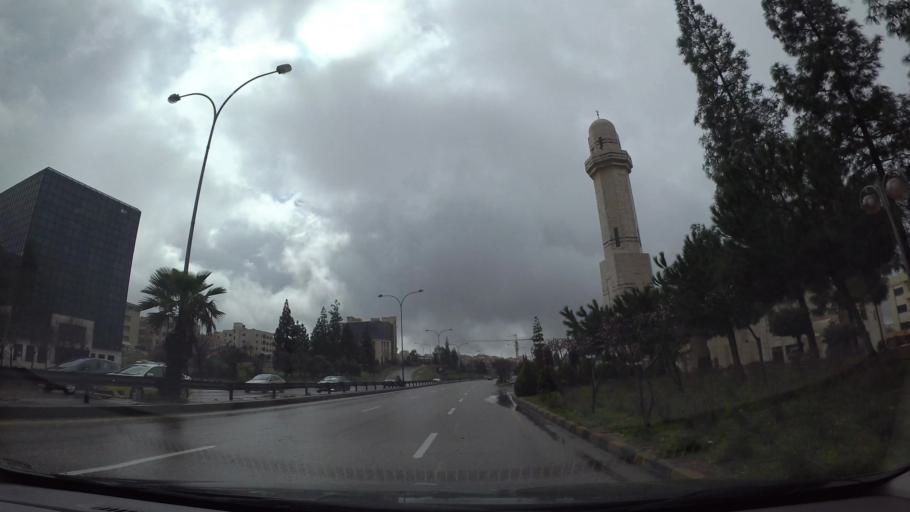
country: JO
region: Amman
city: Wadi as Sir
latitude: 31.9484
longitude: 35.8594
